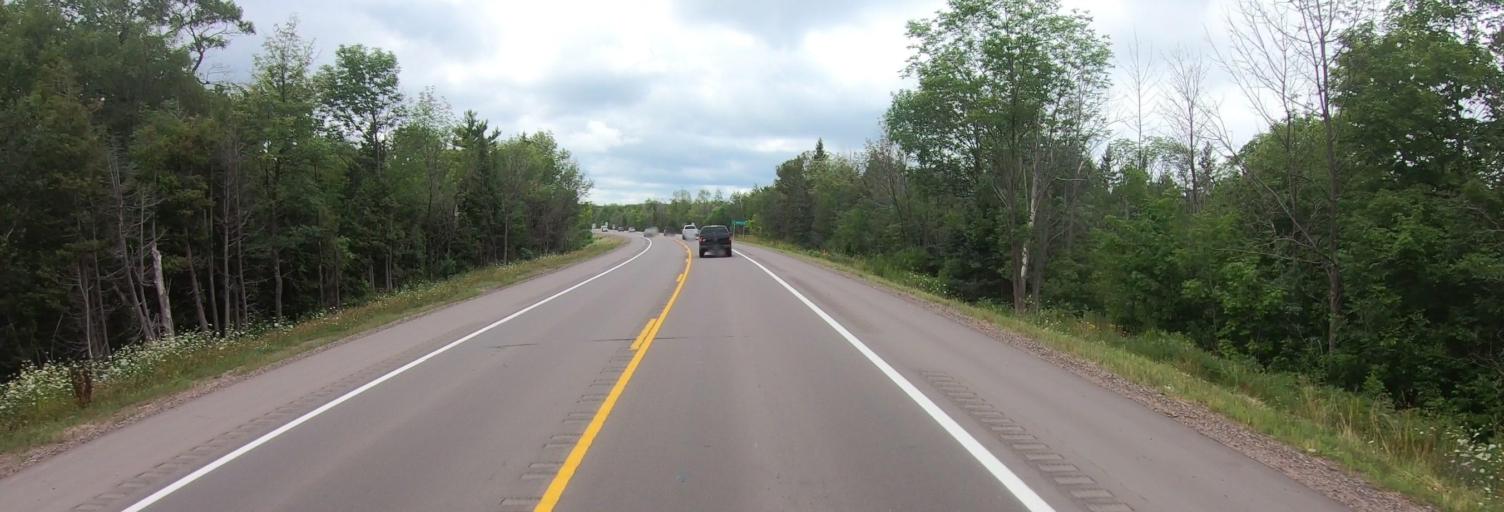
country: US
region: Michigan
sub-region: Houghton County
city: Houghton
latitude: 47.1545
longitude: -88.5591
